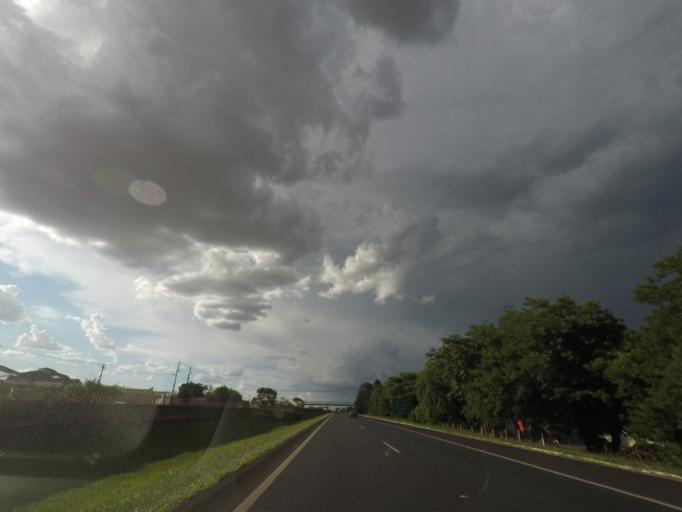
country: BR
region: Sao Paulo
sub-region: Ribeirao Preto
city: Ribeirao Preto
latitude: -21.1269
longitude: -47.7700
